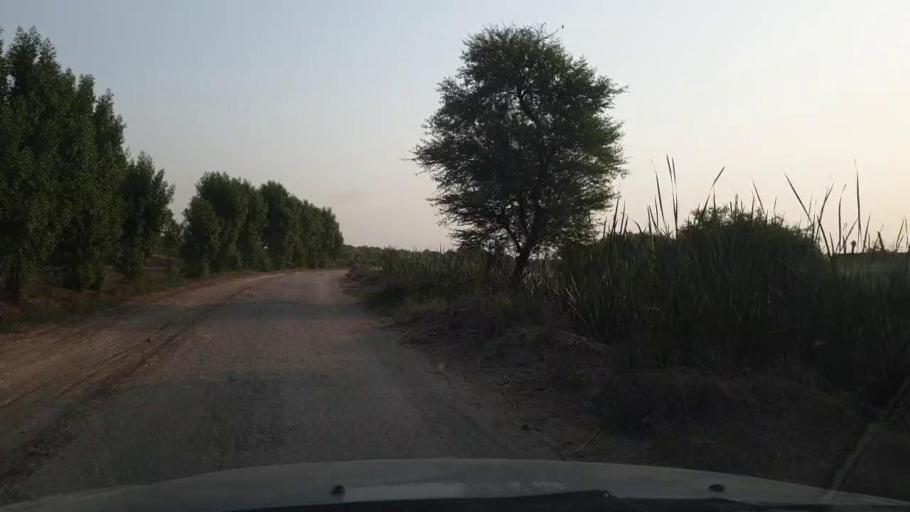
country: PK
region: Sindh
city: Tando Muhammad Khan
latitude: 25.0149
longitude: 68.4382
